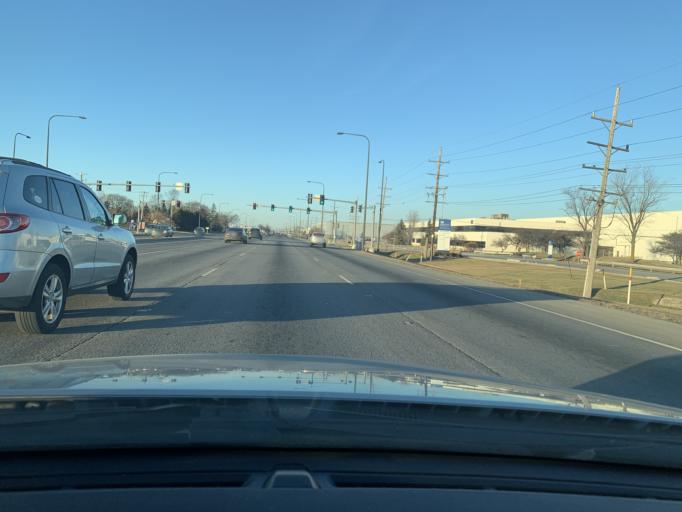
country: US
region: Illinois
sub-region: Cook County
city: Elk Grove Village
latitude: 41.9878
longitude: -87.9592
